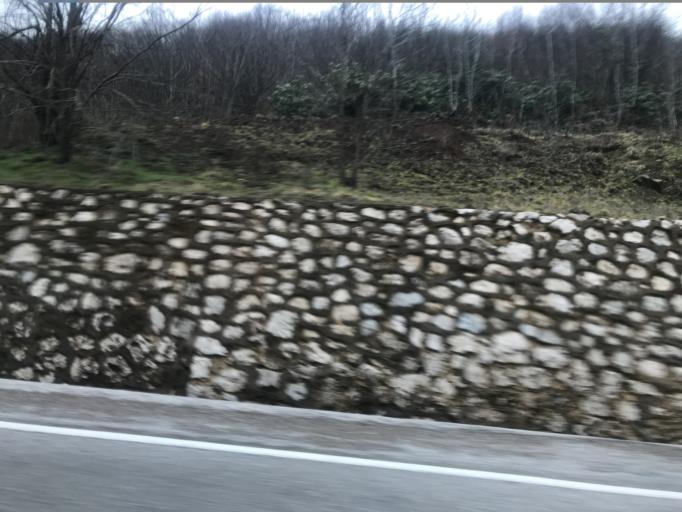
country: TR
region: Bartin
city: Amasra
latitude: 41.7044
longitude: 32.3856
